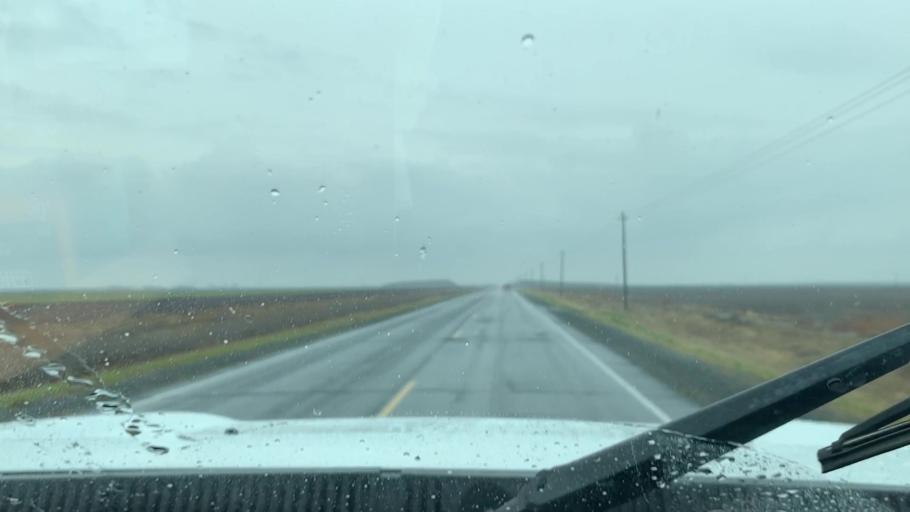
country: US
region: California
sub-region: Tulare County
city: Alpaugh
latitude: 35.9361
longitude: -119.4379
